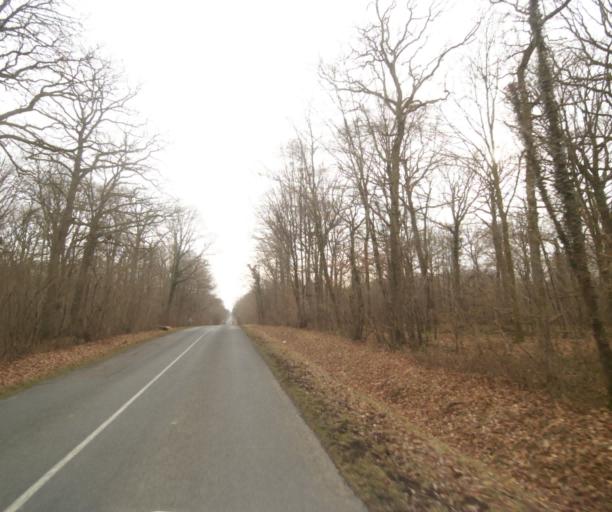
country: FR
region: Champagne-Ardenne
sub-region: Departement de la Marne
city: Pargny-sur-Saulx
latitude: 48.7283
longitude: 4.8674
